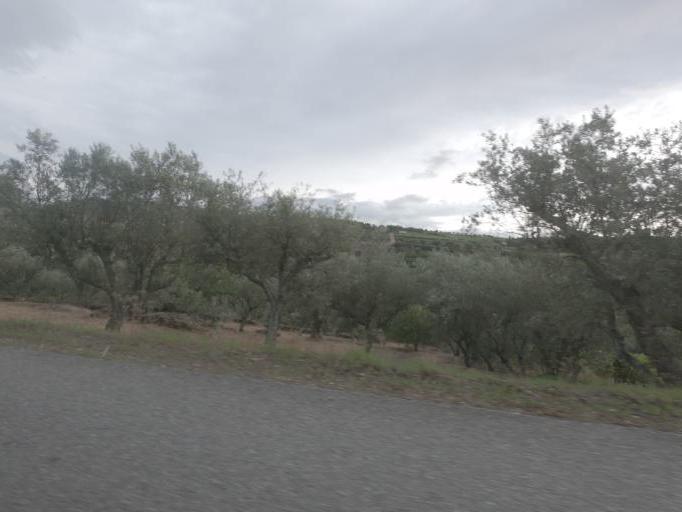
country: PT
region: Vila Real
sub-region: Sabrosa
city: Sabrosa
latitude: 41.2641
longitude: -7.5659
